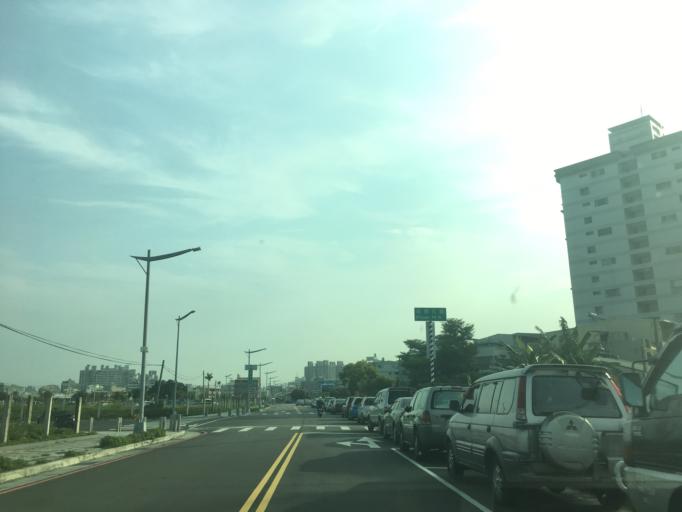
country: TW
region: Taiwan
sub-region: Taichung City
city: Taichung
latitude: 24.1864
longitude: 120.6959
